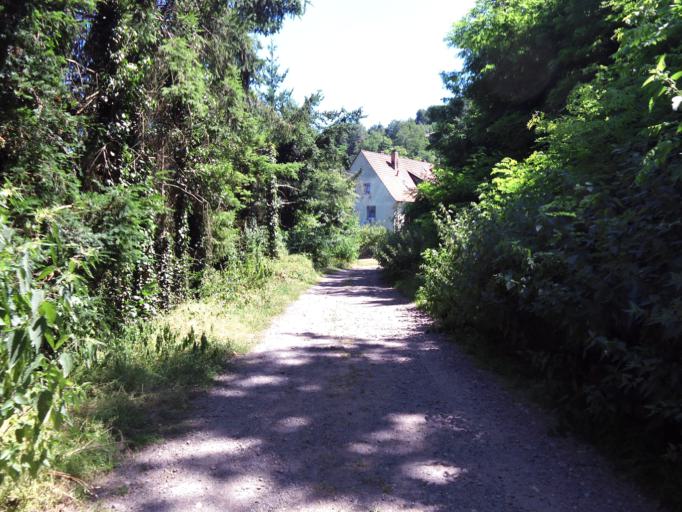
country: DE
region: Rheinland-Pfalz
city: Frankeneck
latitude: 49.3731
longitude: 8.0595
